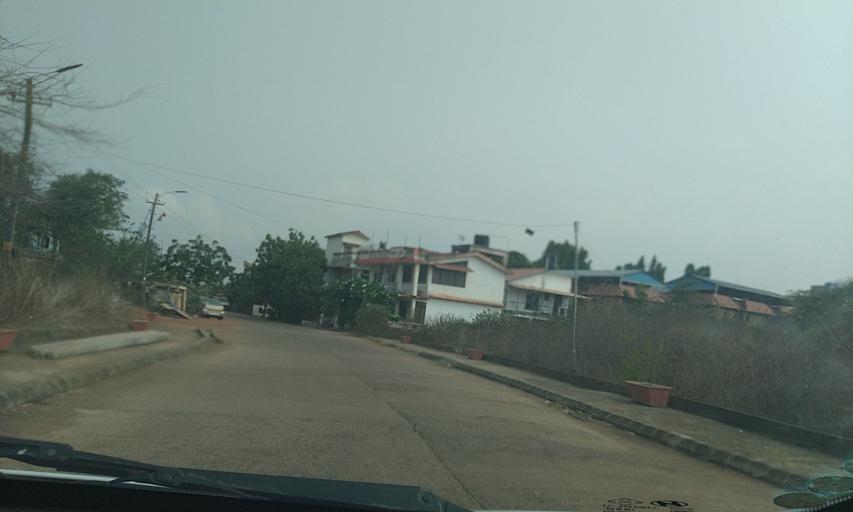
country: IN
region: Goa
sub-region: North Goa
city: Taleigao
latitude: 15.4617
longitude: 73.8173
